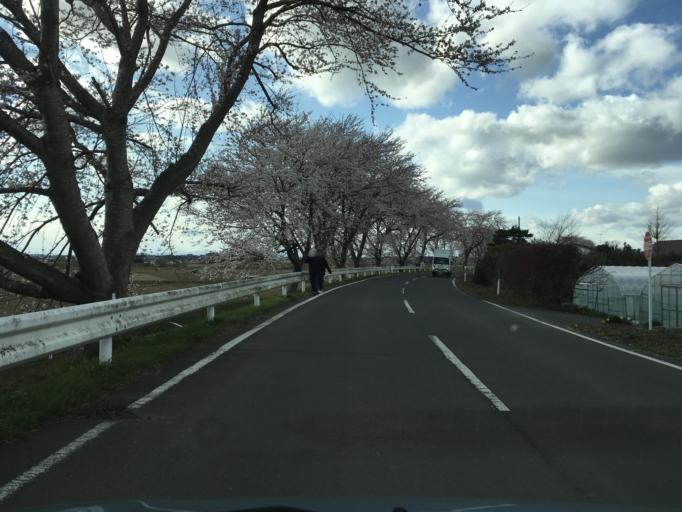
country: JP
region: Miyagi
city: Wakuya
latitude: 38.6457
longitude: 141.1467
